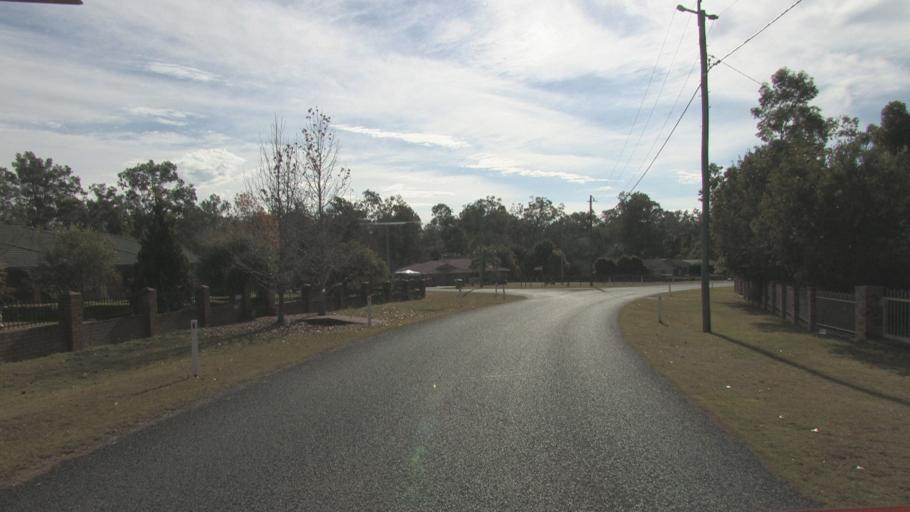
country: AU
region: Queensland
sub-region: Logan
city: Park Ridge South
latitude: -27.7336
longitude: 153.0299
